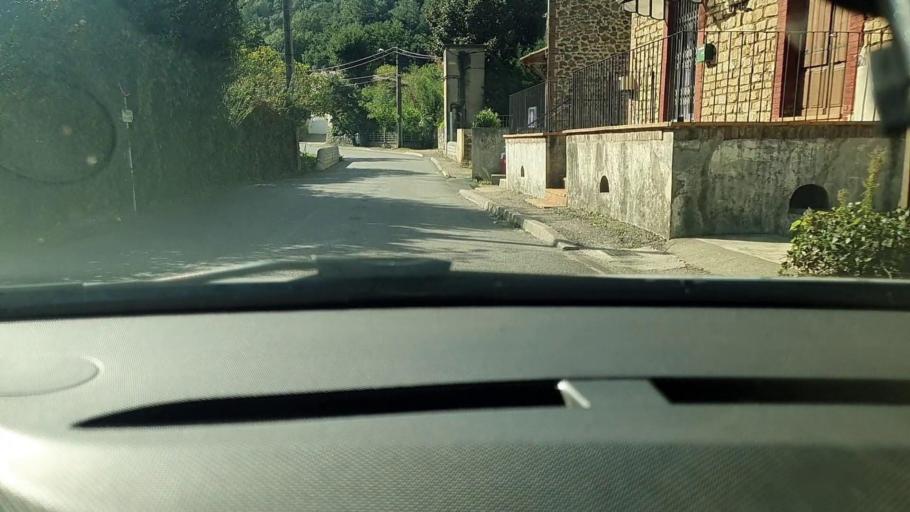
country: FR
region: Languedoc-Roussillon
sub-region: Departement du Gard
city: Molieres-sur-Ceze
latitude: 44.2681
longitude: 4.1490
